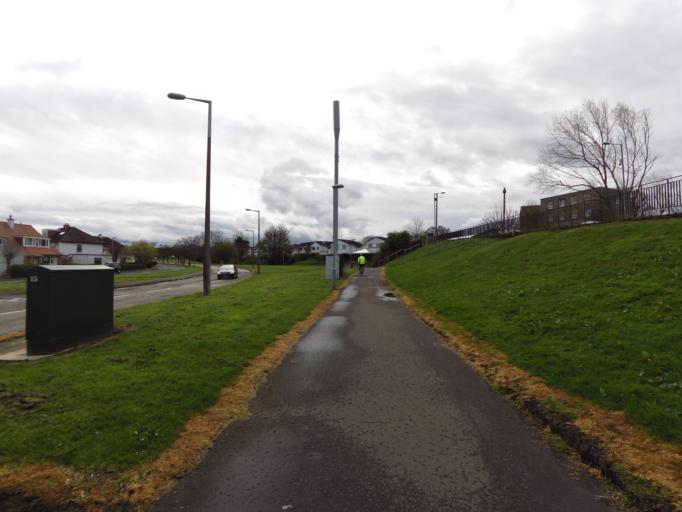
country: GB
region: Scotland
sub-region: Edinburgh
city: Colinton
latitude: 55.9672
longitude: -3.2684
